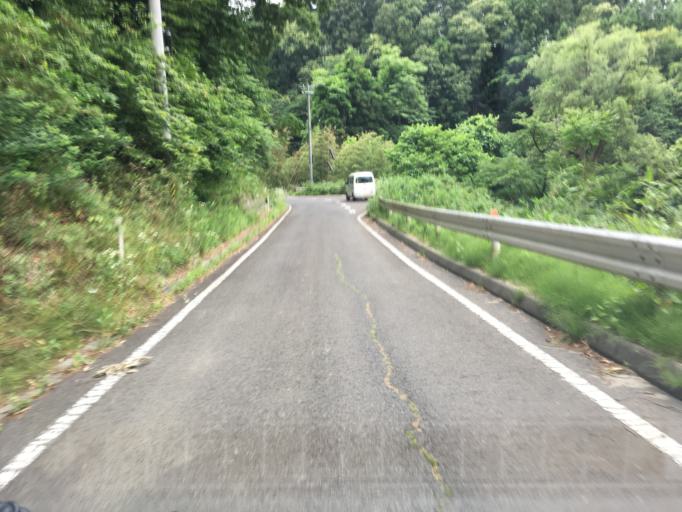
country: JP
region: Fukushima
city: Nihommatsu
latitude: 37.6356
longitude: 140.5263
